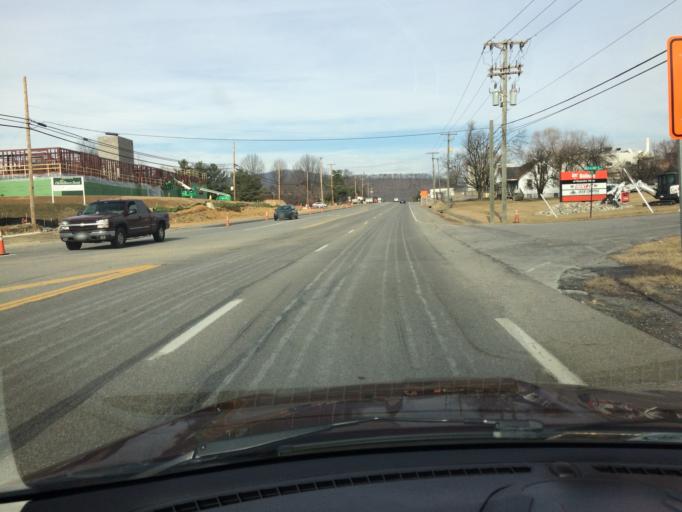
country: US
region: Virginia
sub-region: Roanoke County
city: Hollins
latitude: 37.3510
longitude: -79.9532
